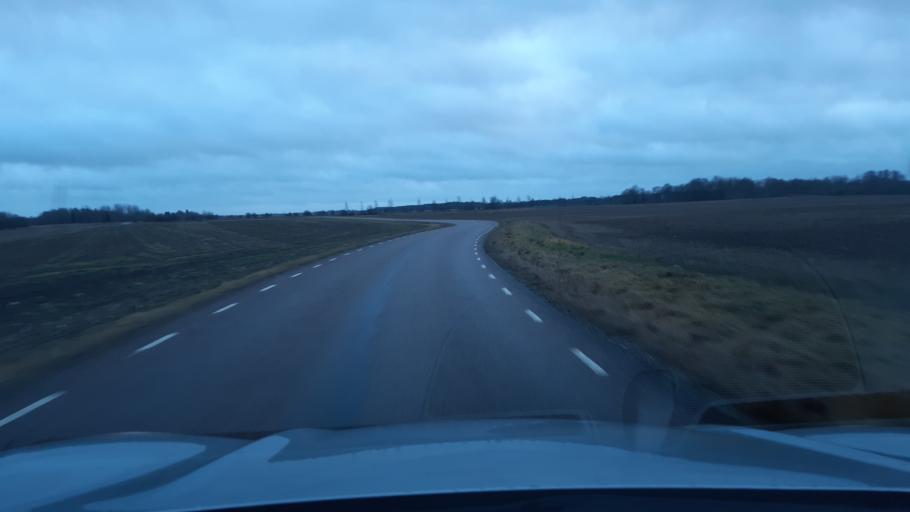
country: EE
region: Raplamaa
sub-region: Rapla vald
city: Rapla
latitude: 59.0126
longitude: 24.7050
